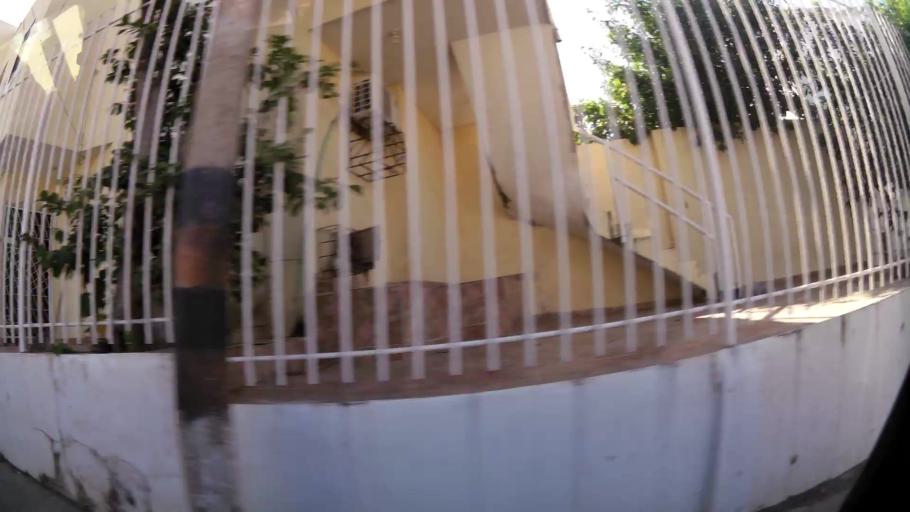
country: CO
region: Bolivar
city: Cartagena
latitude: 10.4211
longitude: -75.5297
